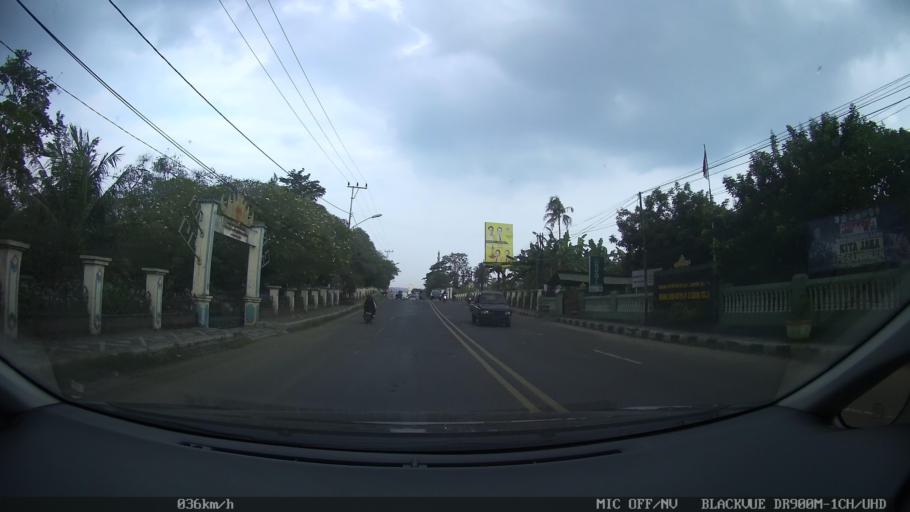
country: ID
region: Lampung
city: Gedongtataan
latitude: -5.3800
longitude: 105.1019
